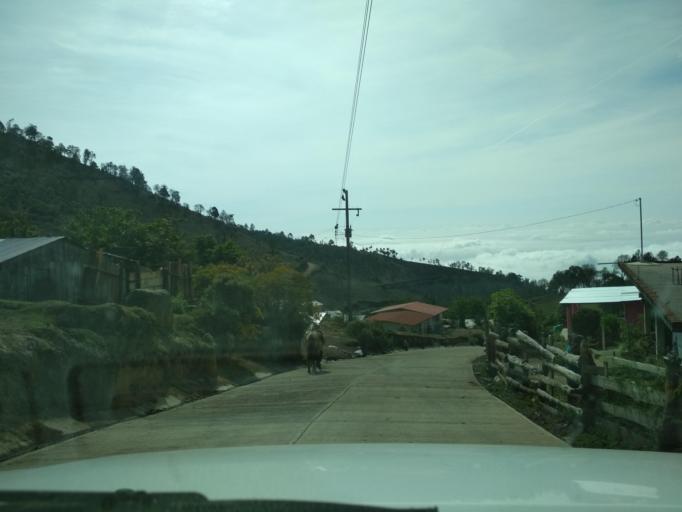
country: MX
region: Veracruz
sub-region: Mariano Escobedo
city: Texmola
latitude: 18.9938
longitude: -97.2235
